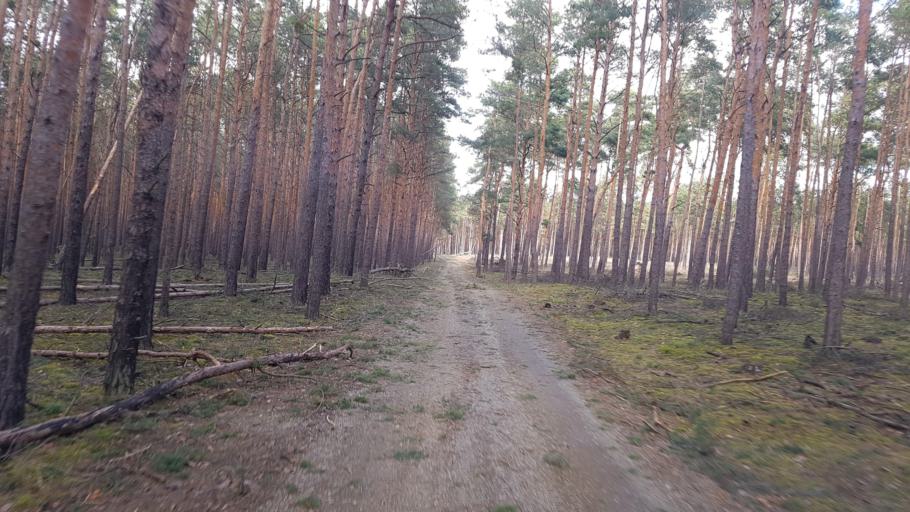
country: DE
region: Brandenburg
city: Schlieben
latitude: 51.6777
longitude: 13.3991
